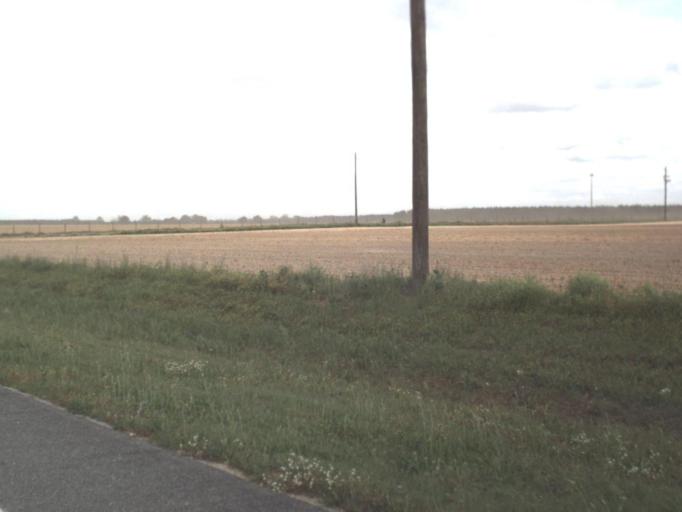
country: US
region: Florida
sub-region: Santa Rosa County
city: Point Baker
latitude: 30.7622
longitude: -87.0930
